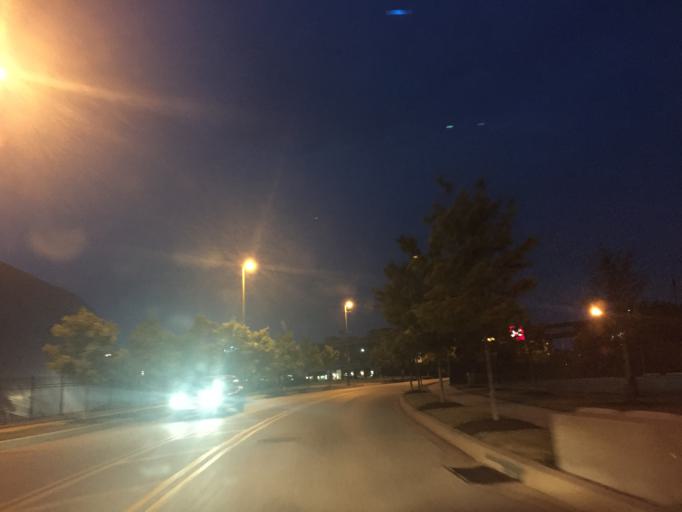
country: US
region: Maryland
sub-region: City of Baltimore
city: Baltimore
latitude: 39.2740
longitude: -76.5942
